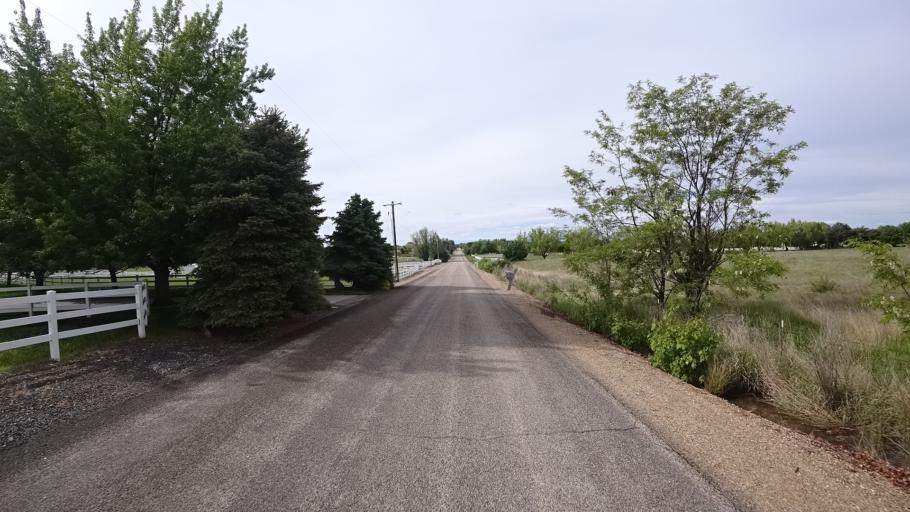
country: US
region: Idaho
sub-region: Ada County
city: Eagle
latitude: 43.7328
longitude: -116.4034
